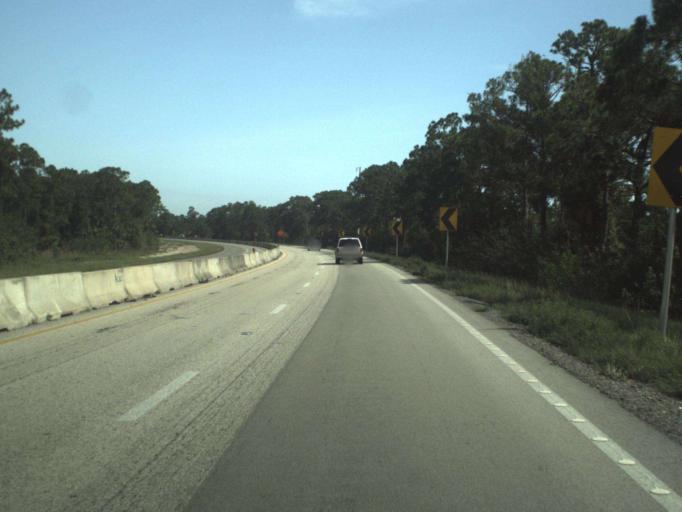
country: US
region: Florida
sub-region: Indian River County
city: Roseland
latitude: 27.8129
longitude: -80.5478
